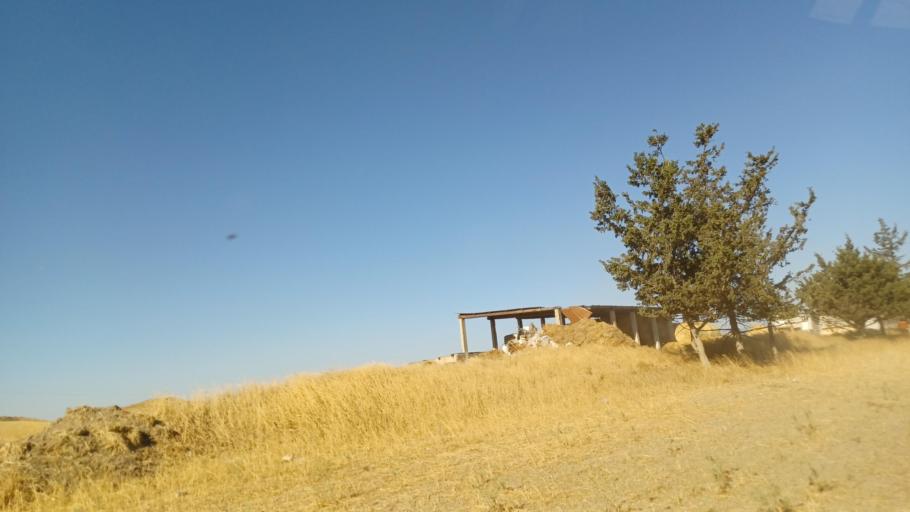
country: CY
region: Larnaka
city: Troulloi
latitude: 35.0105
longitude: 33.6078
